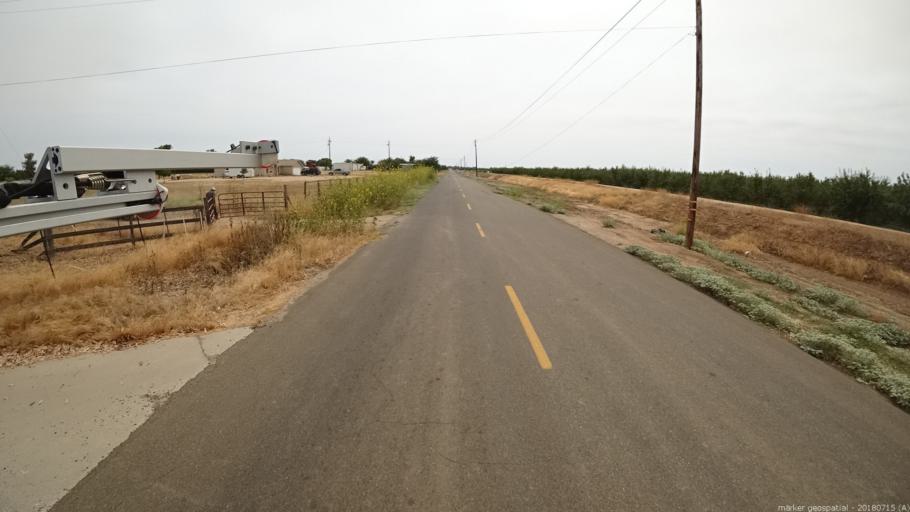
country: US
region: California
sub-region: Madera County
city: Madera Acres
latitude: 37.0255
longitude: -120.1075
